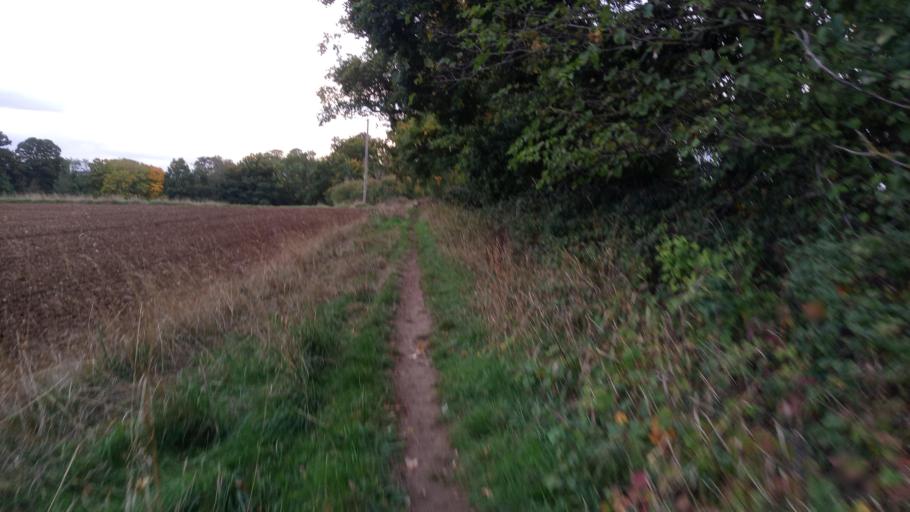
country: GB
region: England
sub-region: Cambridgeshire
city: Linton
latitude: 52.0532
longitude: 0.3058
